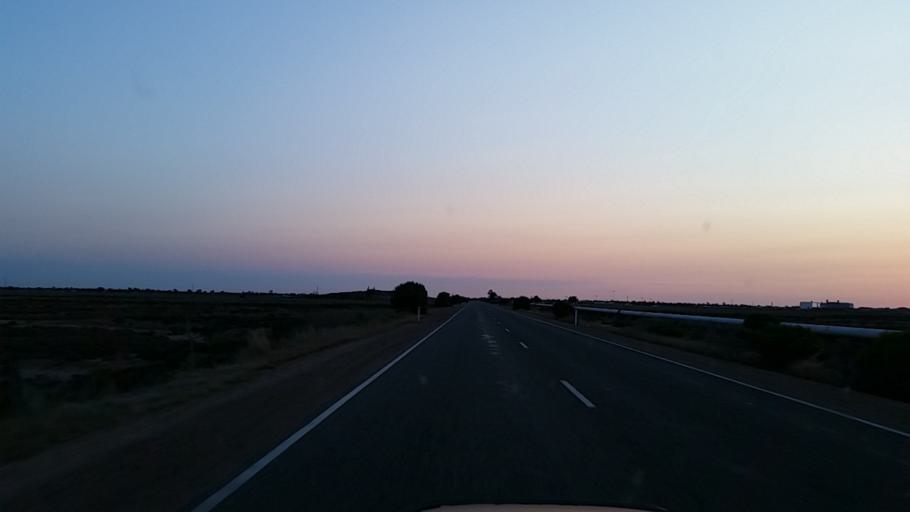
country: AU
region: South Australia
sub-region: Port Pirie City and Dists
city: Solomontown
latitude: -33.1712
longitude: 138.0623
